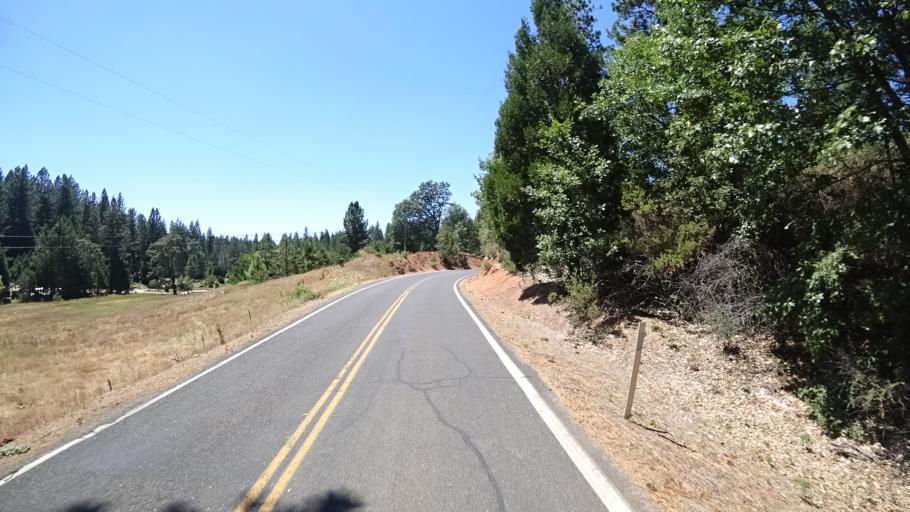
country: US
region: California
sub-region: Calaveras County
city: Mountain Ranch
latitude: 38.3107
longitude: -120.5182
